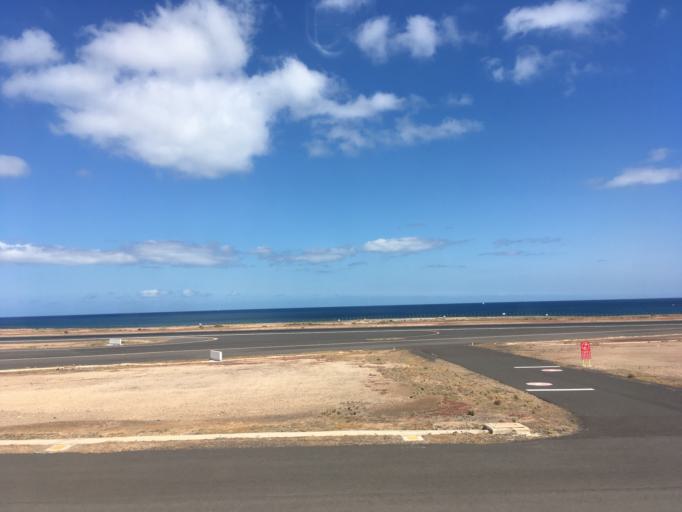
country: ES
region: Canary Islands
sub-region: Provincia de Las Palmas
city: Tias
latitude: 28.9463
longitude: -13.6068
